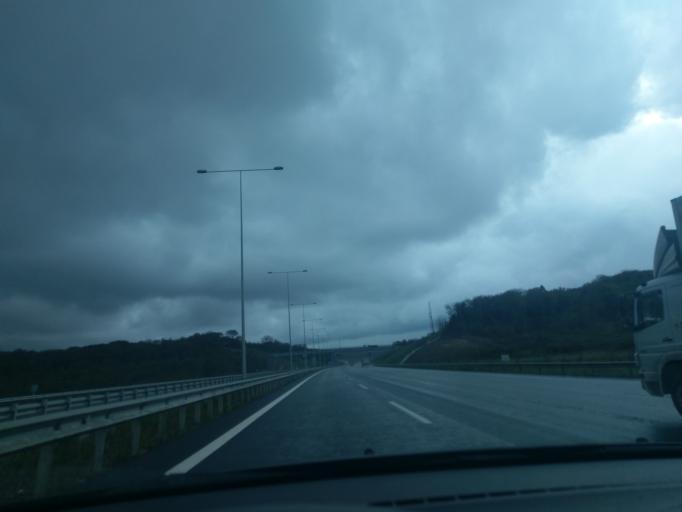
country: TR
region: Istanbul
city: Kemerburgaz
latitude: 41.2348
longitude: 28.9142
